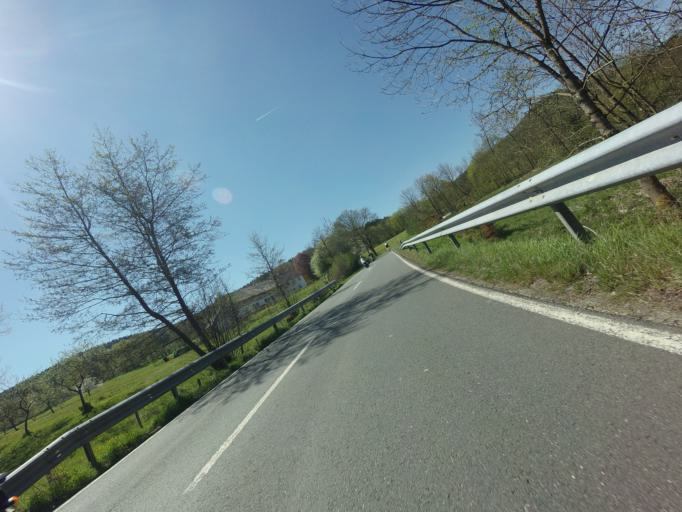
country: DE
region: North Rhine-Westphalia
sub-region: Regierungsbezirk Arnsberg
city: Kirchhundem
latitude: 51.0818
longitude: 8.1825
